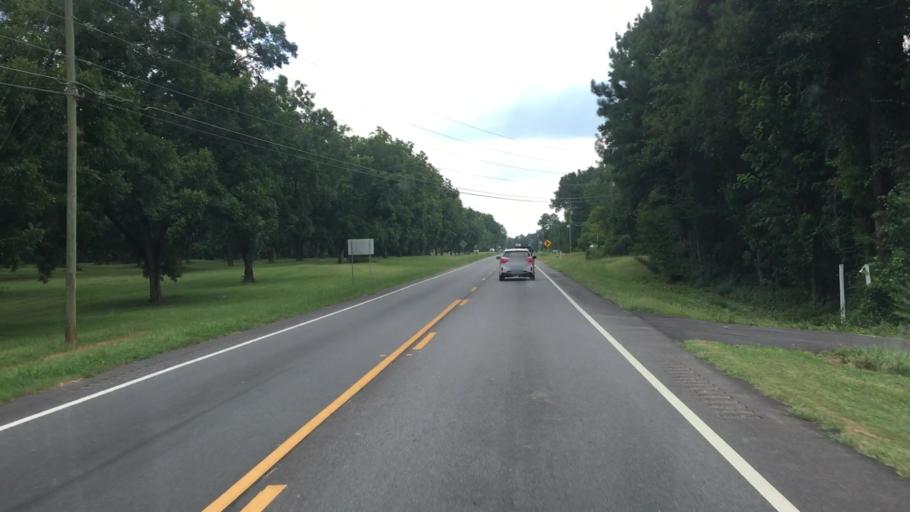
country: US
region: Georgia
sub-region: Putnam County
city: Eatonton
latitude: 33.3646
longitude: -83.3855
